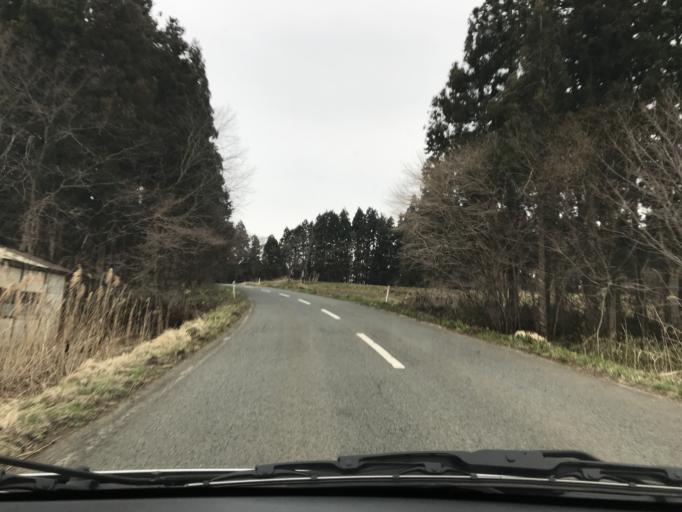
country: JP
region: Iwate
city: Mizusawa
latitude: 39.0930
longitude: 141.0687
